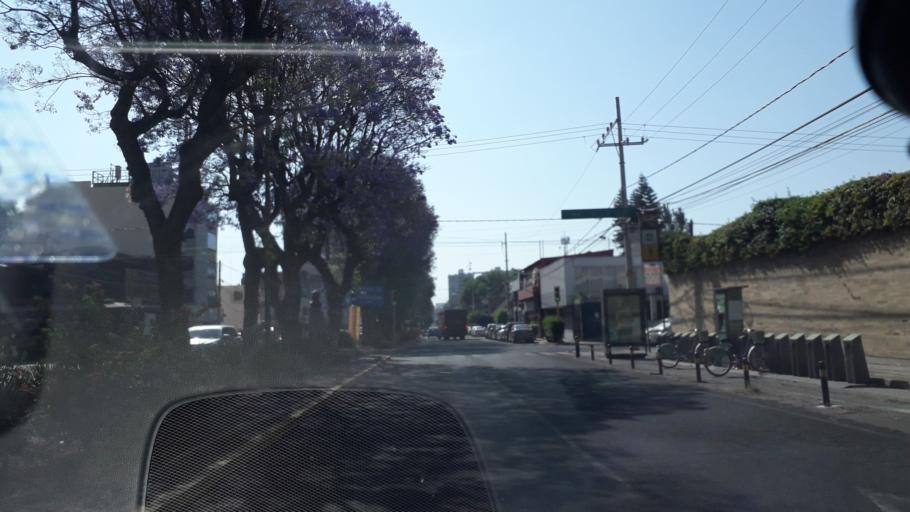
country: MX
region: Puebla
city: Puebla
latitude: 19.0296
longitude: -98.2118
